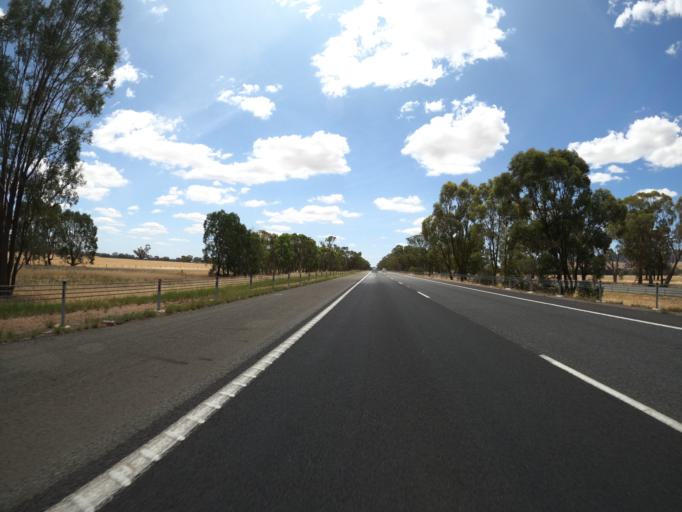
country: AU
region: Victoria
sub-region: Benalla
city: Benalla
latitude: -36.7023
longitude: 145.6512
